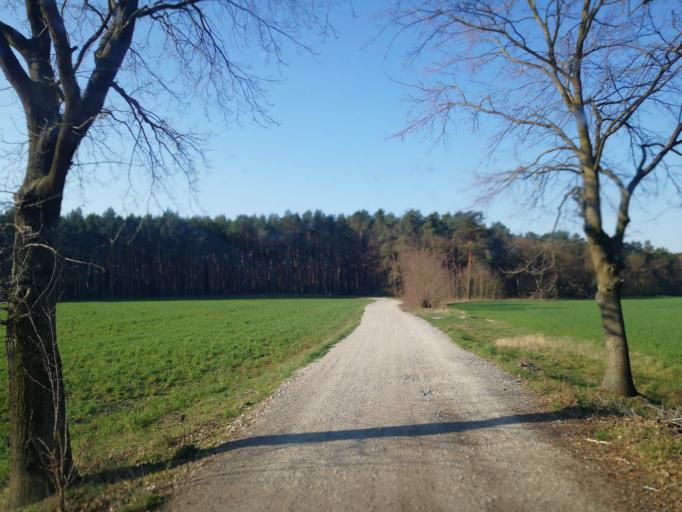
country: DE
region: Brandenburg
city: Drahnsdorf
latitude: 51.9317
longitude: 13.5827
